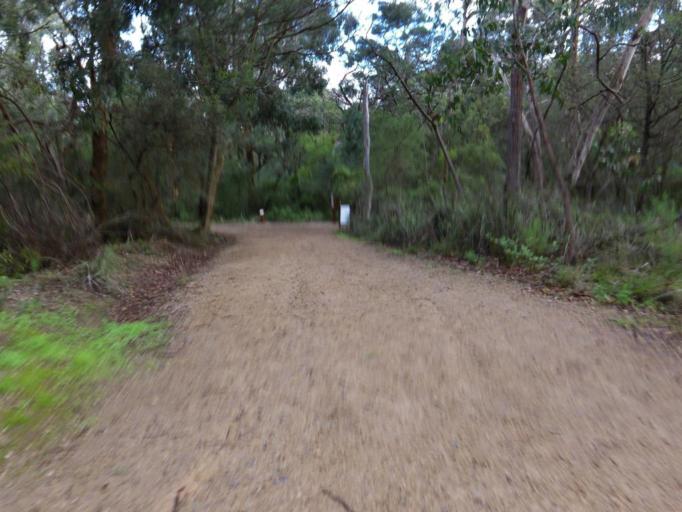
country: AU
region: Victoria
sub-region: Monash
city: Notting Hill
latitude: -37.8819
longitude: 145.1358
